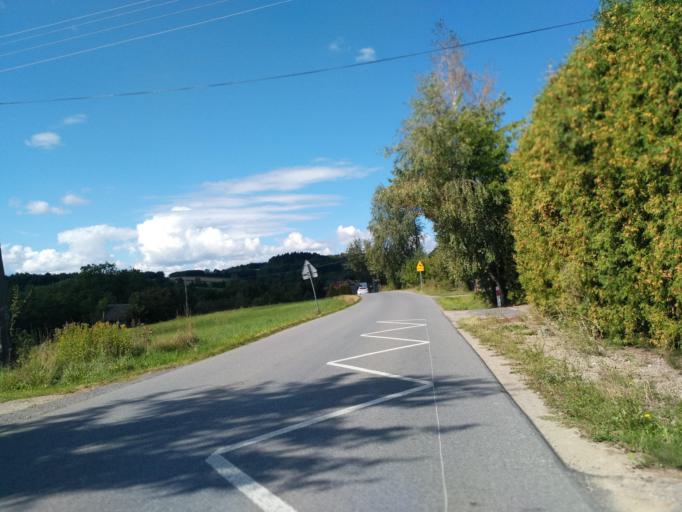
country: PL
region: Subcarpathian Voivodeship
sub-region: Powiat jasielski
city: Skolyszyn
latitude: 49.7807
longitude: 21.3606
